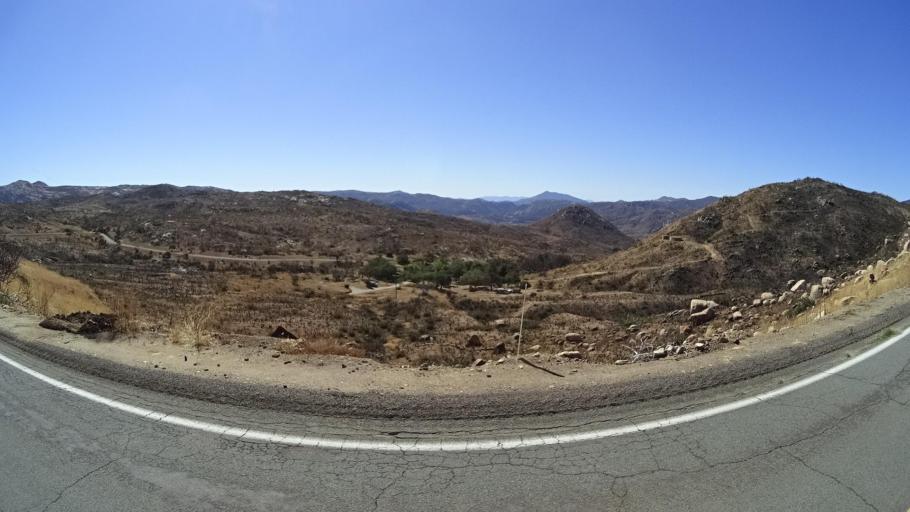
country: US
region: California
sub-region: San Diego County
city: Descanso
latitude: 32.7467
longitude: -116.6745
